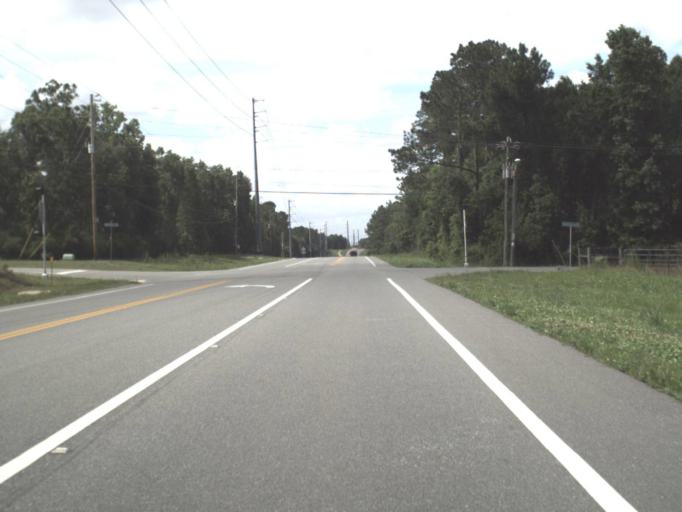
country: US
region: Florida
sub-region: Clay County
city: Middleburg
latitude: 30.0256
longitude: -81.8976
